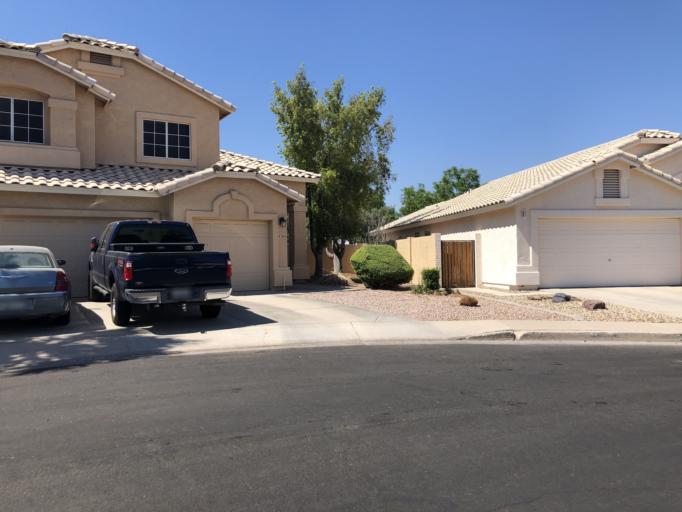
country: US
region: Arizona
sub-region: Maricopa County
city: San Carlos
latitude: 33.3192
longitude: -111.9148
